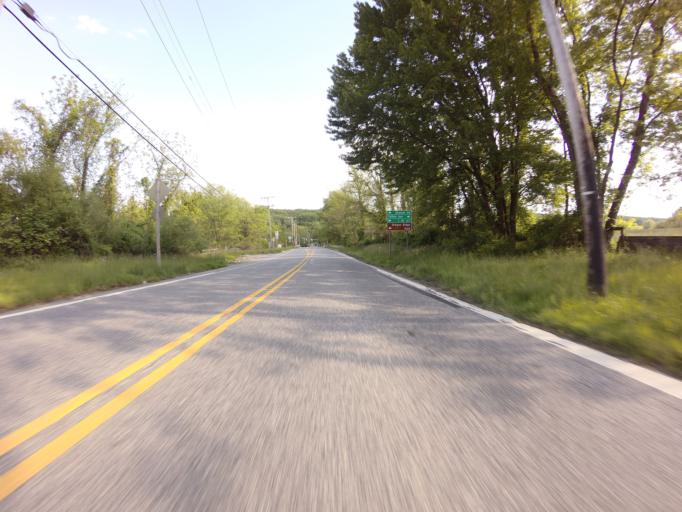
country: US
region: Maryland
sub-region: Baltimore County
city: Hunt Valley
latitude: 39.5010
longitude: -76.7099
